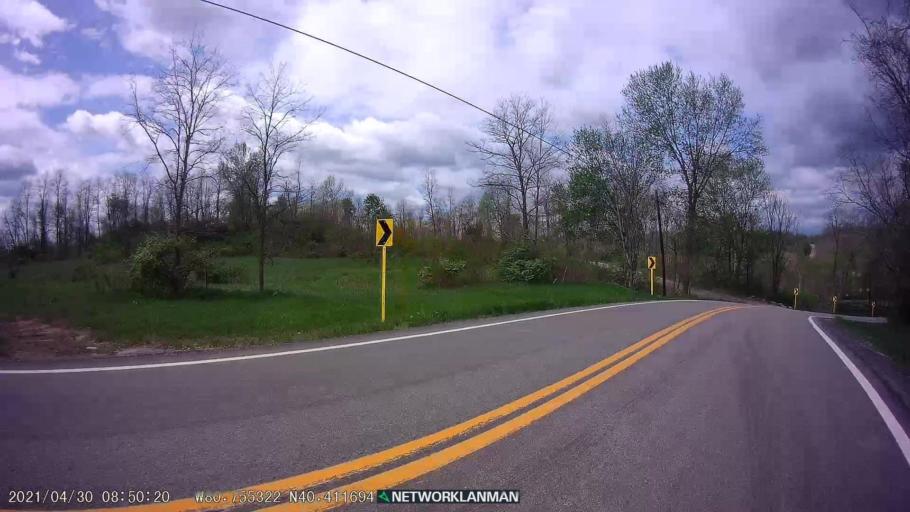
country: US
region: Ohio
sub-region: Jefferson County
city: Wintersville
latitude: 40.4119
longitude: -80.7552
